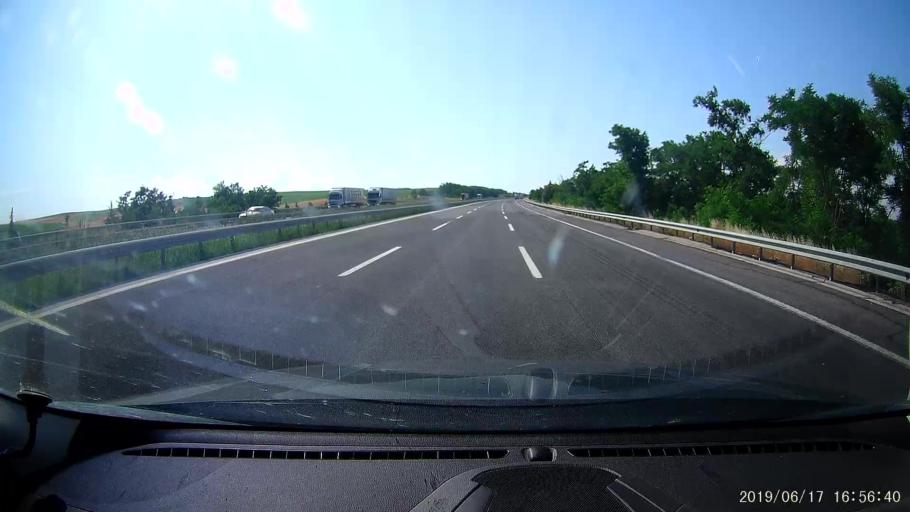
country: TR
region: Edirne
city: Haskoy
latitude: 41.5894
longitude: 26.9308
